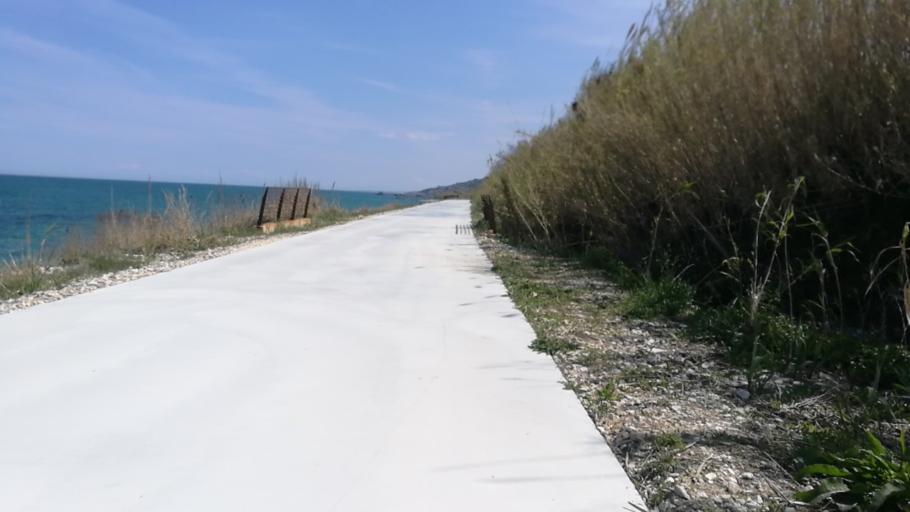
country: IT
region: Abruzzo
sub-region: Provincia di Chieti
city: Marina di San Vito
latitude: 42.3228
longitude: 14.4291
